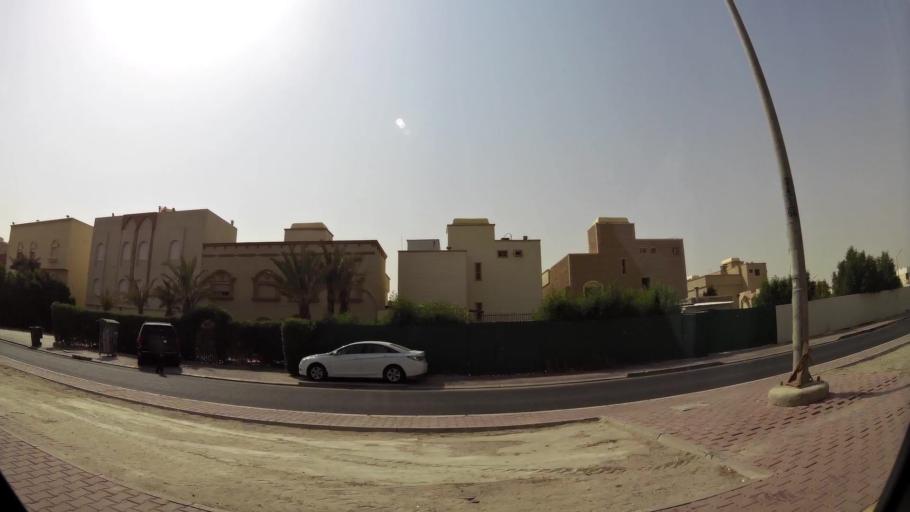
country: KW
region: Muhafazat al Jahra'
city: Al Jahra'
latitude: 29.3191
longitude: 47.7261
